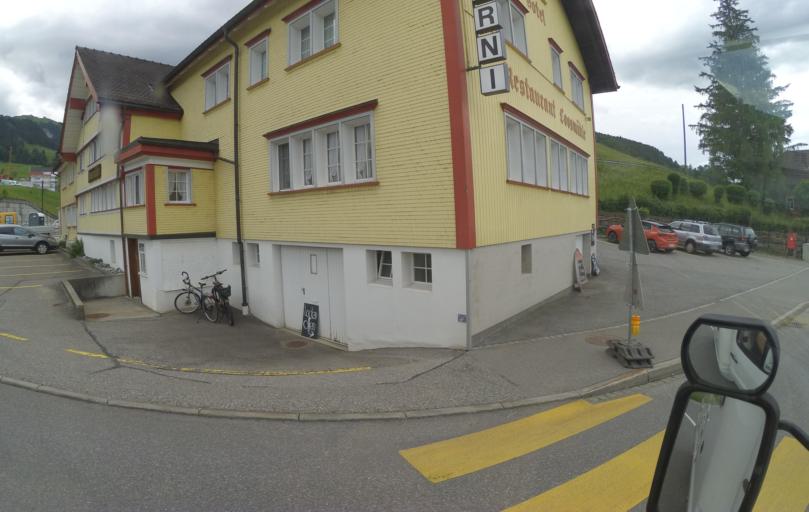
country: CH
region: Appenzell Innerrhoden
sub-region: Appenzell Inner Rhodes
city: Appenzell
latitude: 47.3077
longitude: 9.4360
